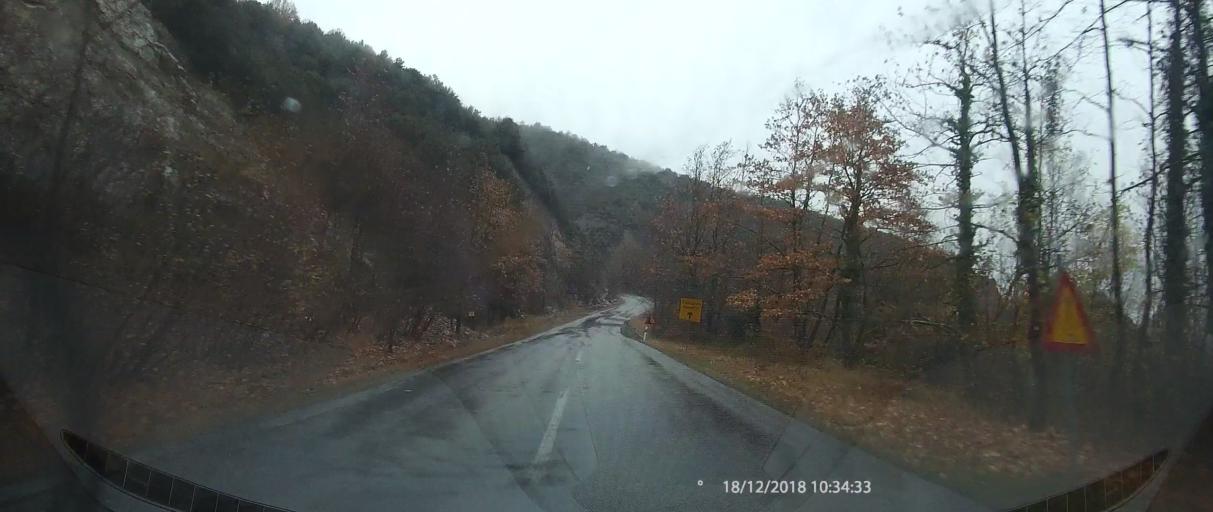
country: GR
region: Central Macedonia
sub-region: Nomos Pierias
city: Kato Milia
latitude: 40.2083
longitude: 22.3015
